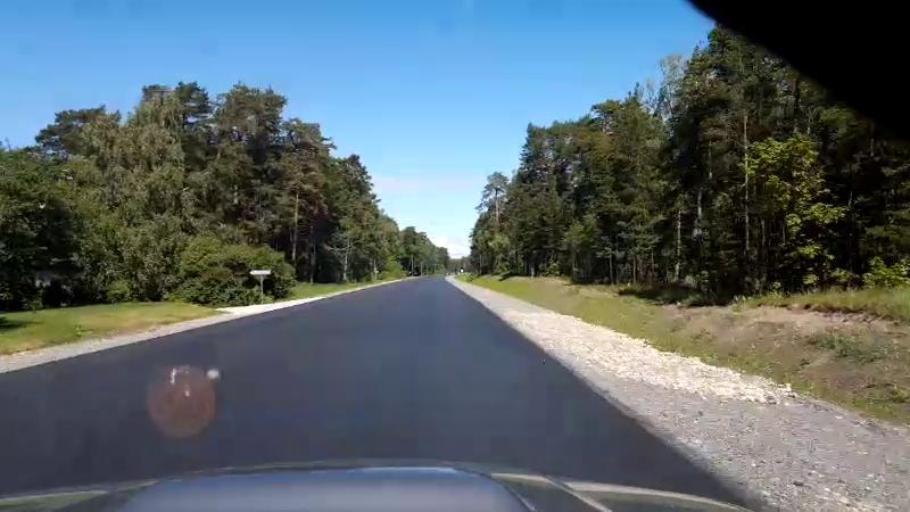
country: LV
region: Salacgrivas
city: Ainazi
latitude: 57.8142
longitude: 24.3473
